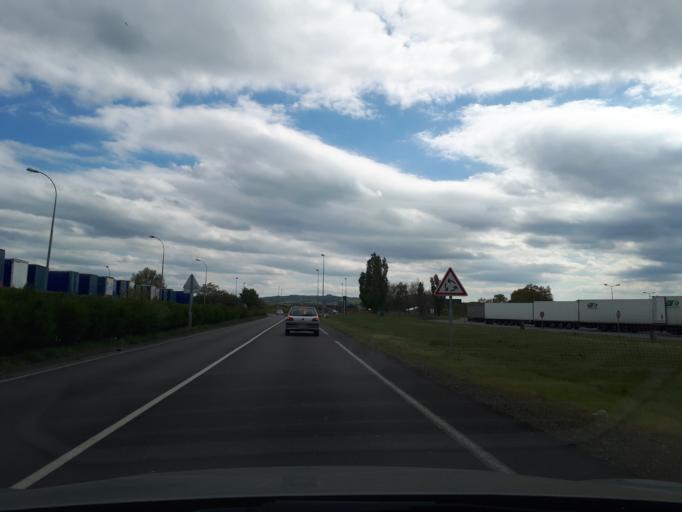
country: FR
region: Rhone-Alpes
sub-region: Departement de la Loire
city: Veauche
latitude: 45.5478
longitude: 4.3058
